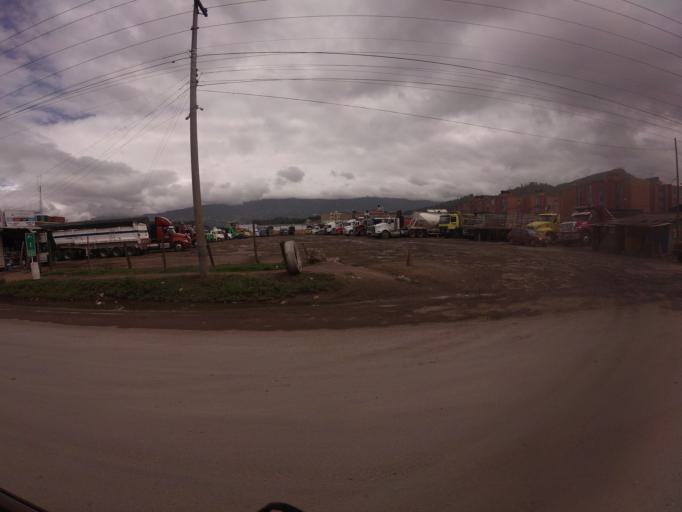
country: CO
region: Boyaca
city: Duitama
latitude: 5.8100
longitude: -73.0175
